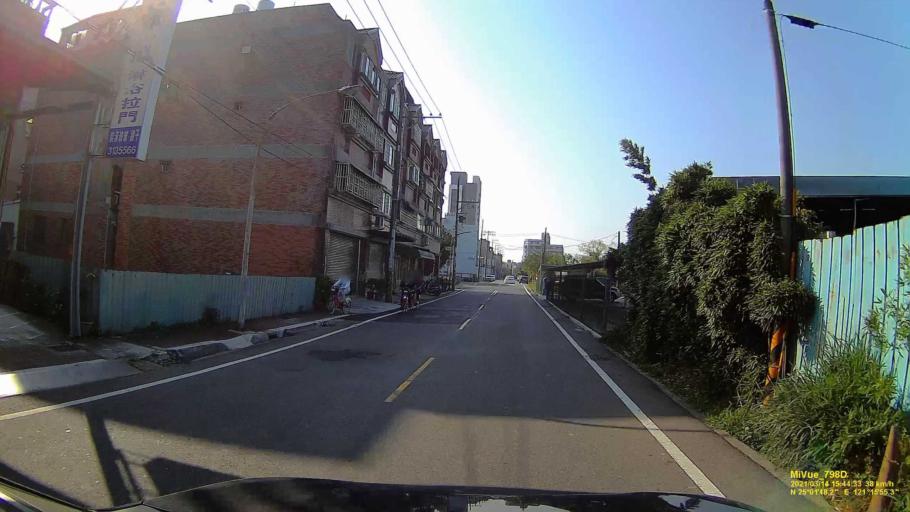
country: TW
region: Taiwan
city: Taoyuan City
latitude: 25.0219
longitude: 121.2651
